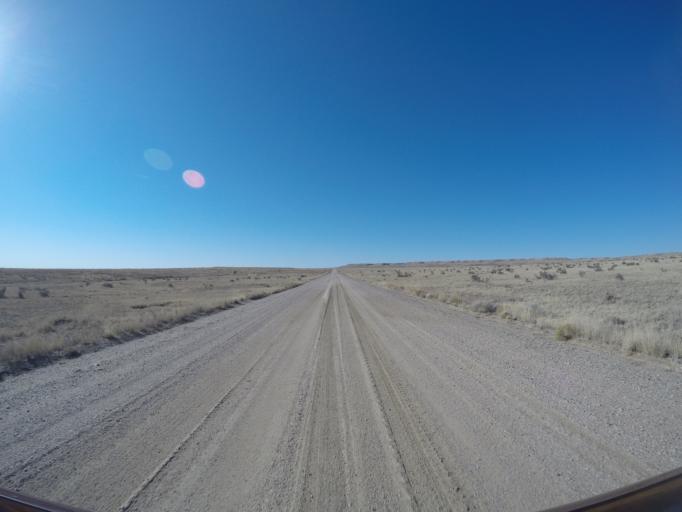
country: US
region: Colorado
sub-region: Otero County
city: La Junta
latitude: 37.7735
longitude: -103.5568
